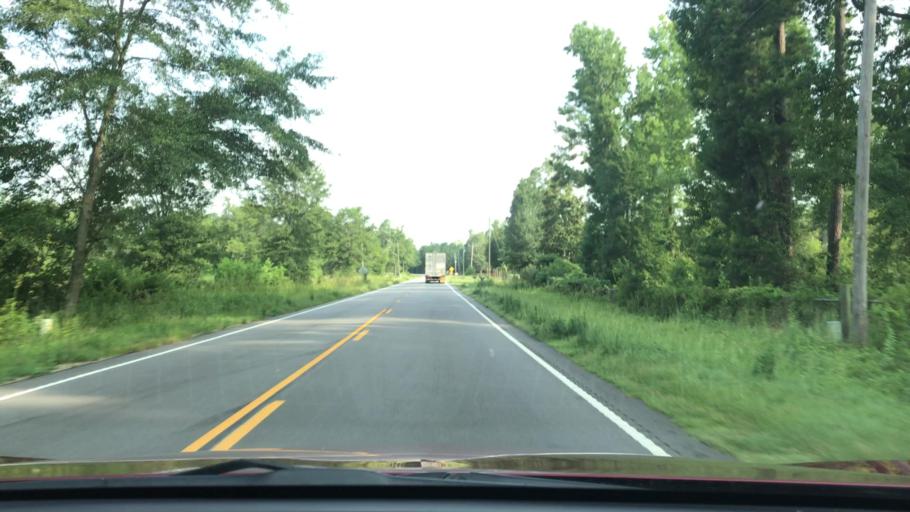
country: US
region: South Carolina
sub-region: Barnwell County
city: Blackville
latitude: 33.5576
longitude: -81.1660
